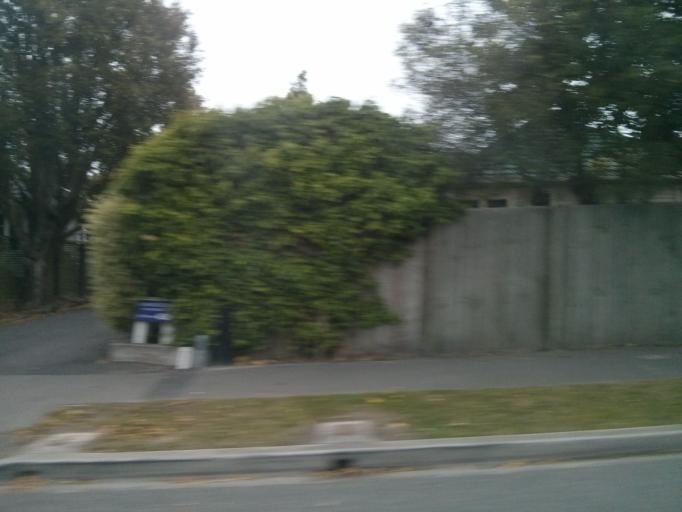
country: NZ
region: Canterbury
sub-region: Christchurch City
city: Christchurch
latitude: -43.5055
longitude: 172.6024
